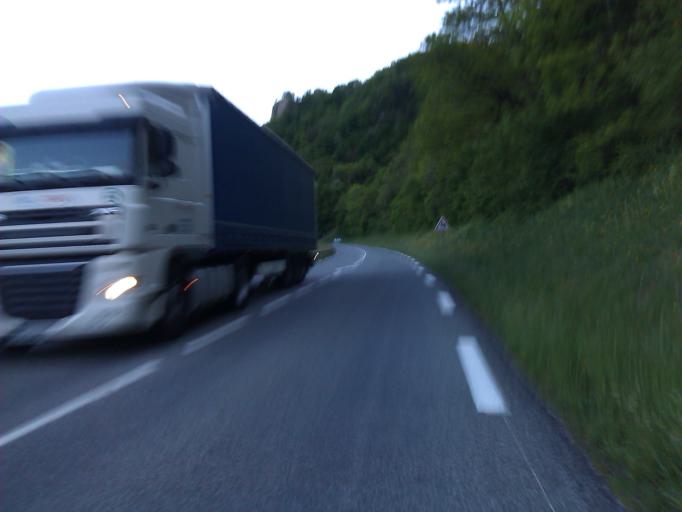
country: FR
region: Franche-Comte
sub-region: Departement du Doubs
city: Baume-les-Dames
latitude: 47.3662
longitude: 6.4175
